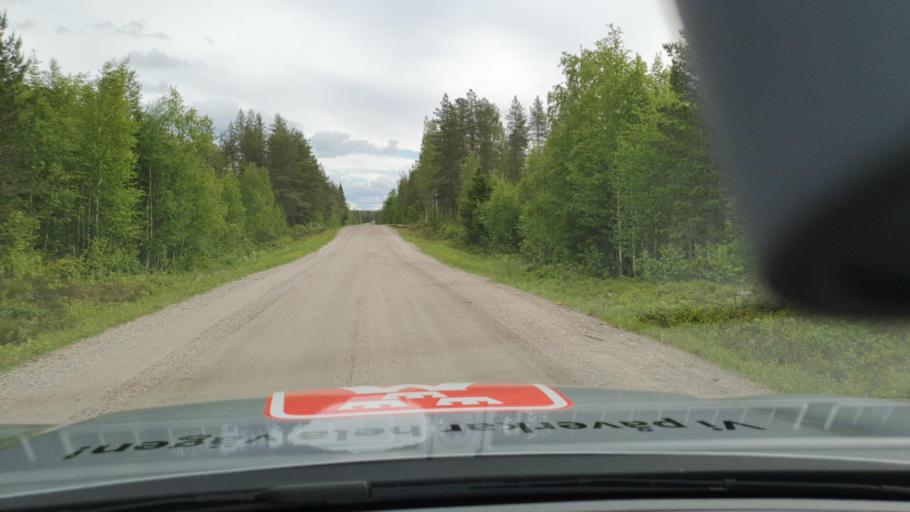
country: FI
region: Lapland
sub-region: Torniolaakso
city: Ylitornio
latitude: 65.9516
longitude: 23.5758
